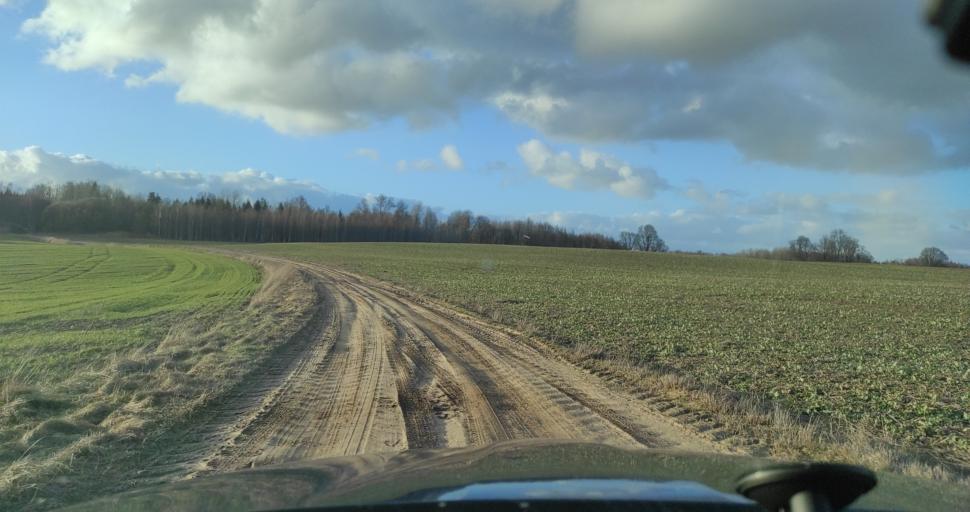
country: LV
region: Aizpute
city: Aizpute
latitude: 56.8685
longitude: 21.7590
